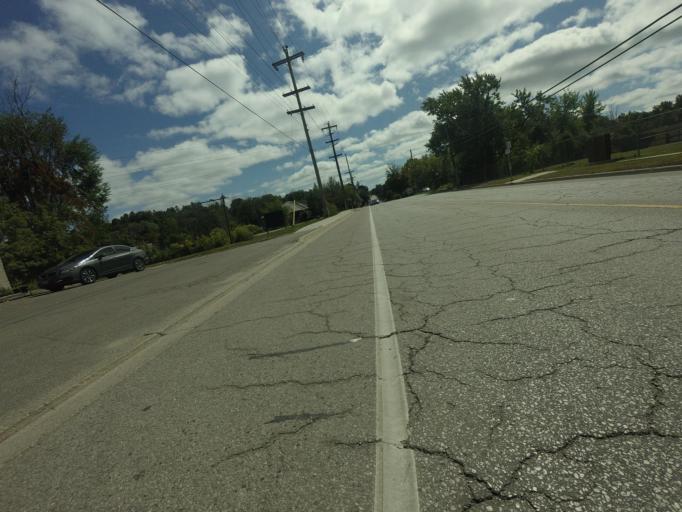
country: CA
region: Ontario
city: Uxbridge
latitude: 44.1144
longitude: -79.1227
